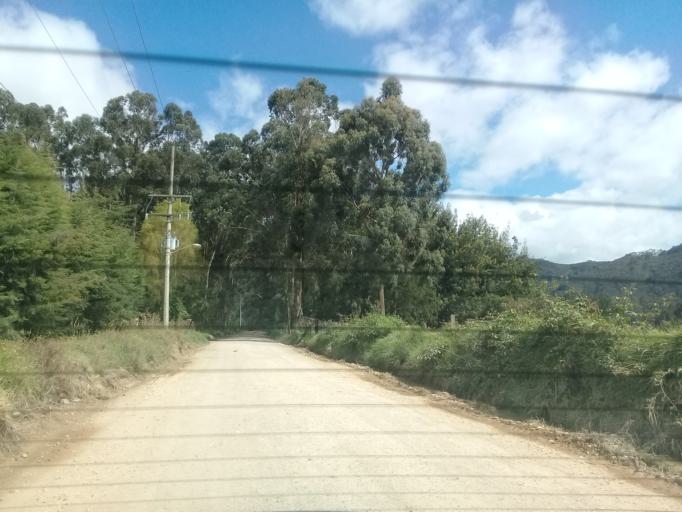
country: CO
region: Cundinamarca
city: El Rosal
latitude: 4.8575
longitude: -74.2073
